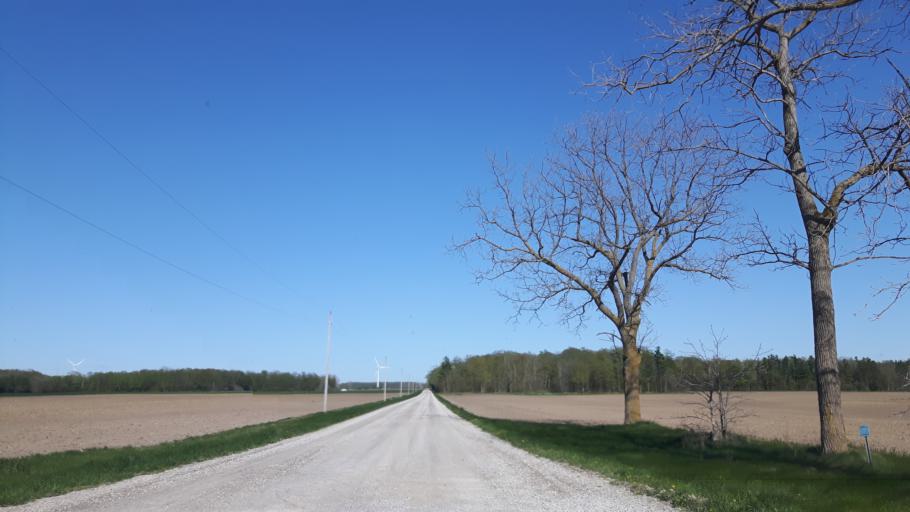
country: CA
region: Ontario
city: Bluewater
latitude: 43.5101
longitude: -81.6941
